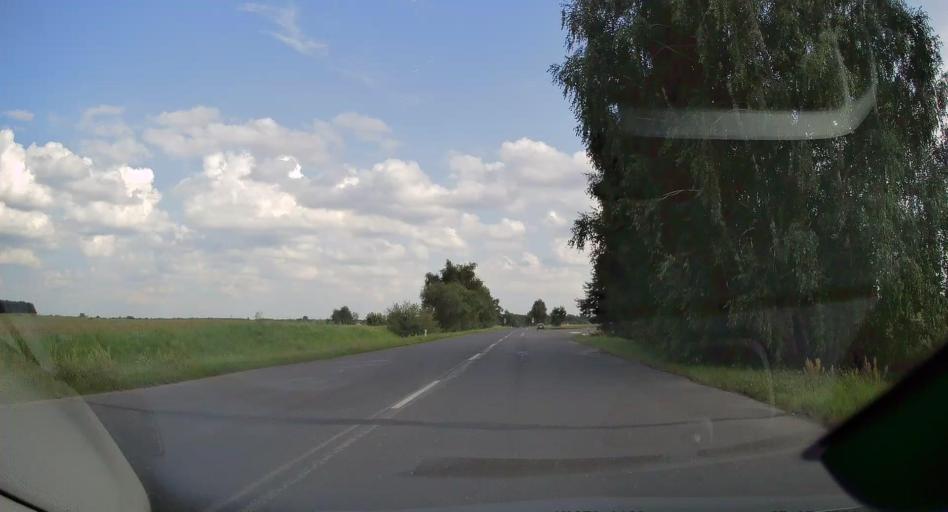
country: PL
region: Lodz Voivodeship
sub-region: Powiat tomaszowski
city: Rzeczyca
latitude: 51.6490
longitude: 20.2808
